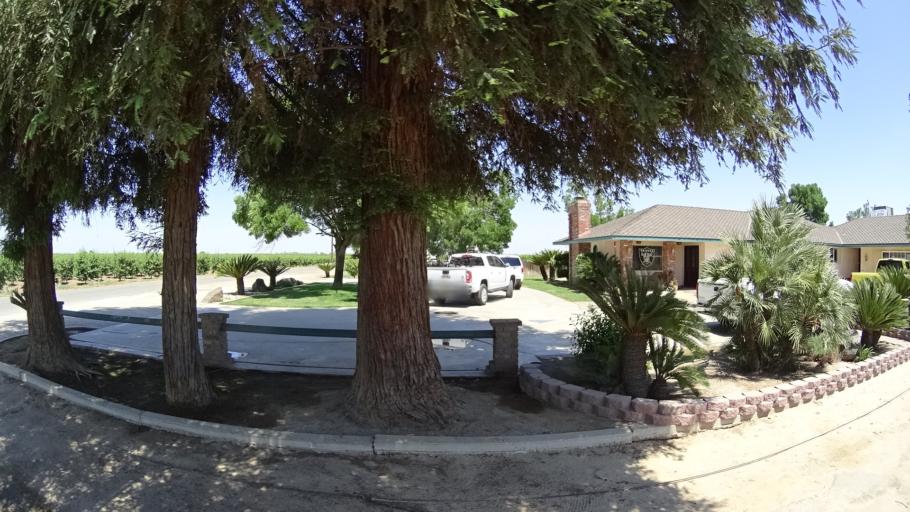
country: US
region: California
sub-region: Fresno County
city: Kingsburg
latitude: 36.4742
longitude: -119.5819
